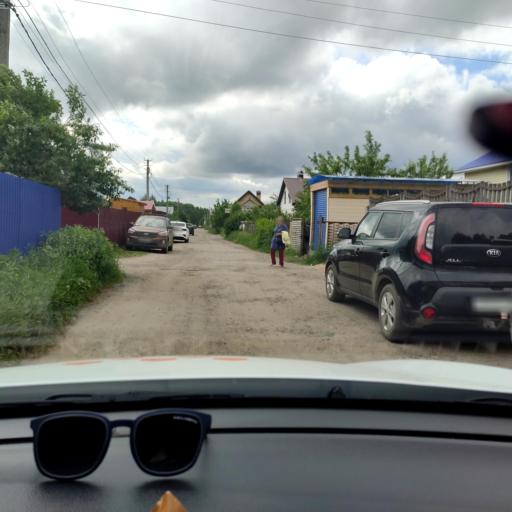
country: RU
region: Tatarstan
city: Vysokaya Gora
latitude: 55.9270
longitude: 49.1610
